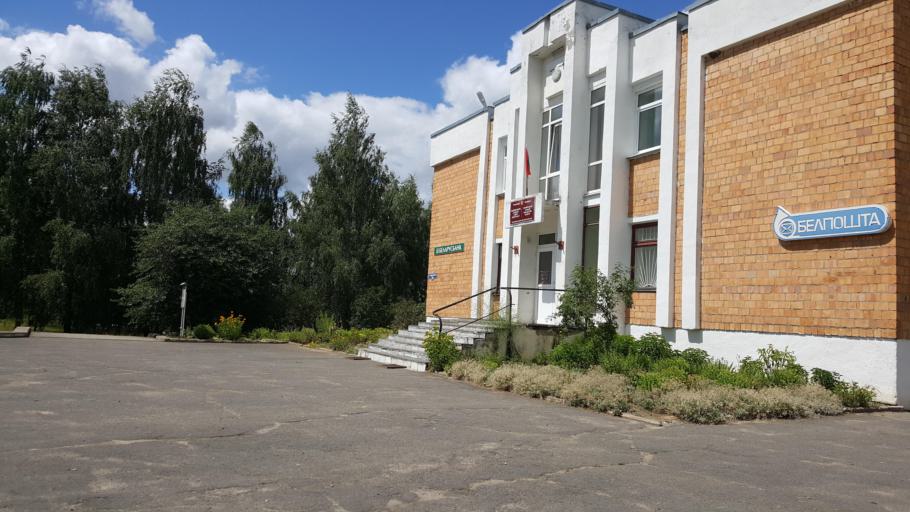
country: BY
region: Brest
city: Kamyanyets
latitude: 52.3195
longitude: 23.9300
